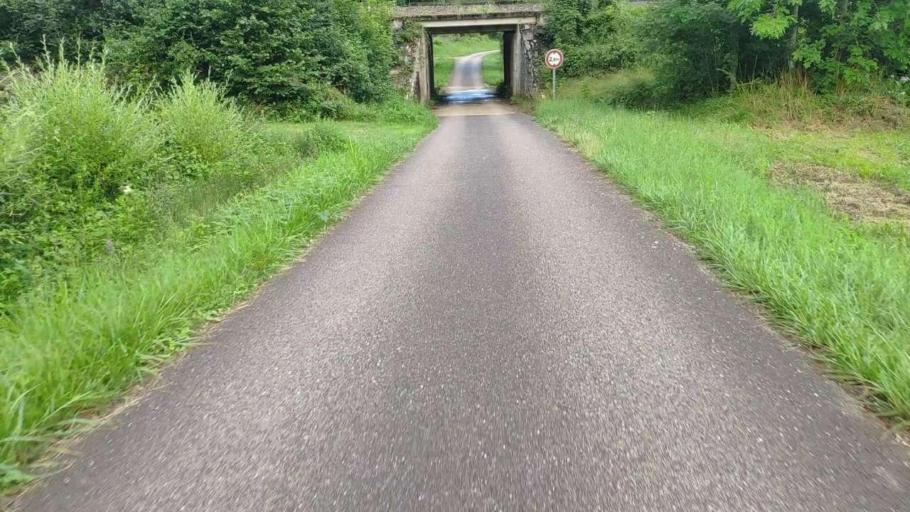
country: FR
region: Franche-Comte
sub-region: Departement du Jura
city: Poligny
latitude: 46.7958
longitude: 5.6010
